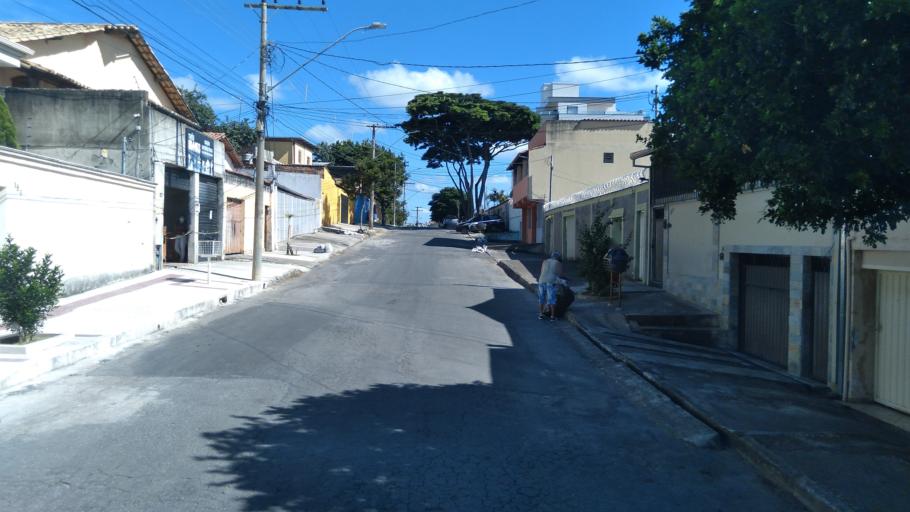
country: BR
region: Minas Gerais
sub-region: Belo Horizonte
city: Belo Horizonte
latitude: -19.8547
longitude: -43.9142
